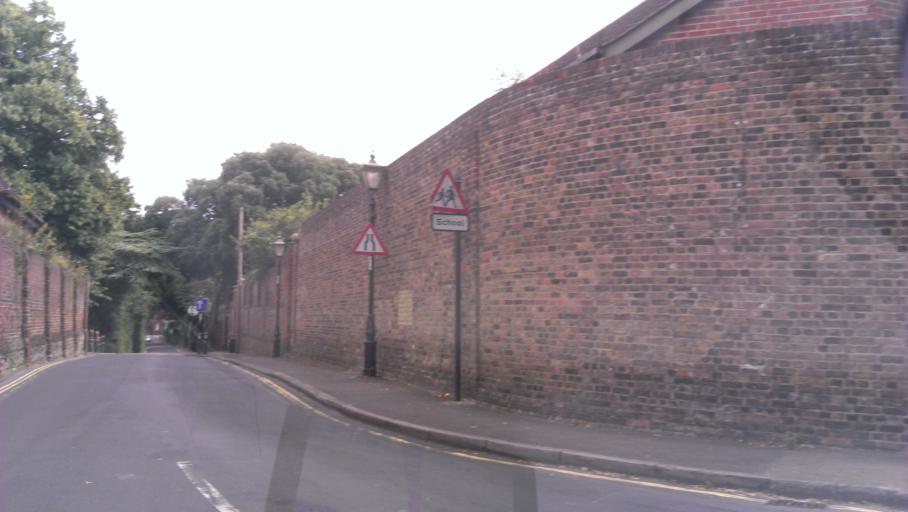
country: GB
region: England
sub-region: Medway
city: Rochester
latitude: 51.3872
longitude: 0.5013
